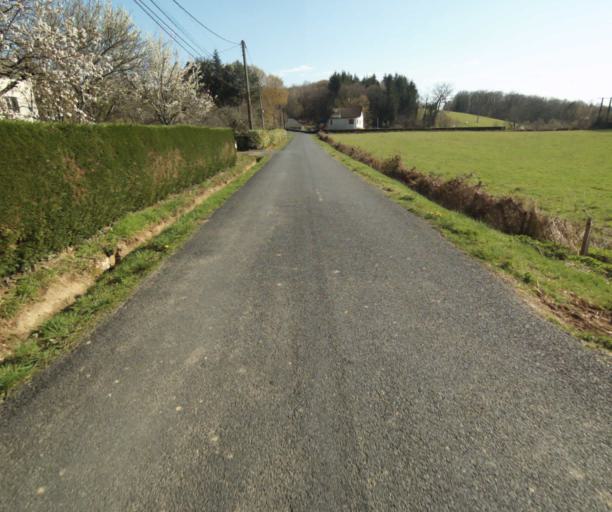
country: FR
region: Limousin
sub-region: Departement de la Correze
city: Saint-Mexant
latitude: 45.3083
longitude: 1.6149
